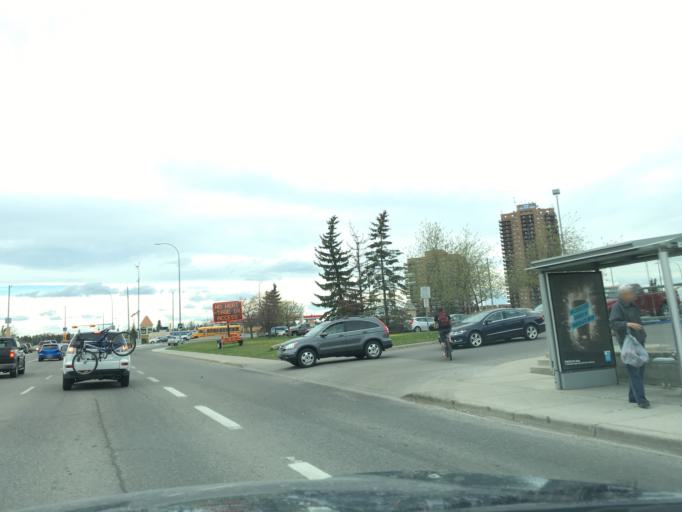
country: CA
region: Alberta
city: Calgary
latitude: 50.9651
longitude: -114.0696
